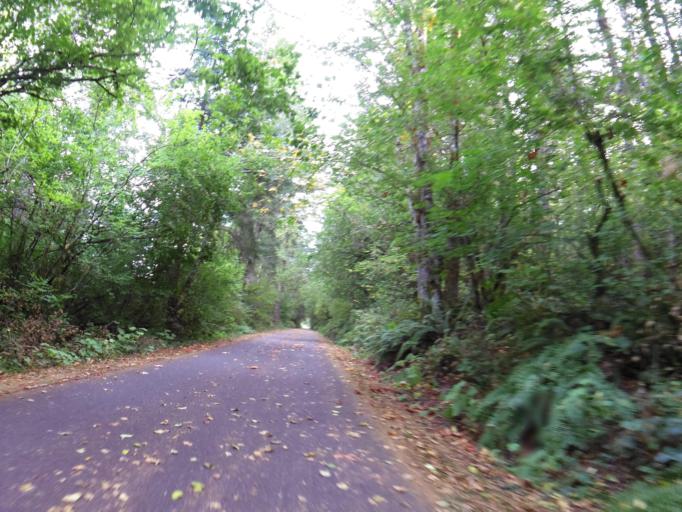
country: US
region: Washington
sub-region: Thurston County
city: Lacey
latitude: 46.9713
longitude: -122.8127
